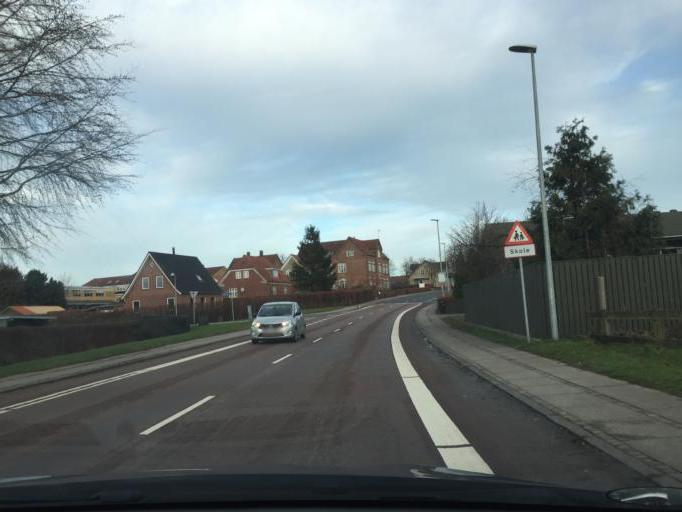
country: DK
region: South Denmark
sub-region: Faaborg-Midtfyn Kommune
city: Ringe
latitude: 55.2333
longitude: 10.4722
